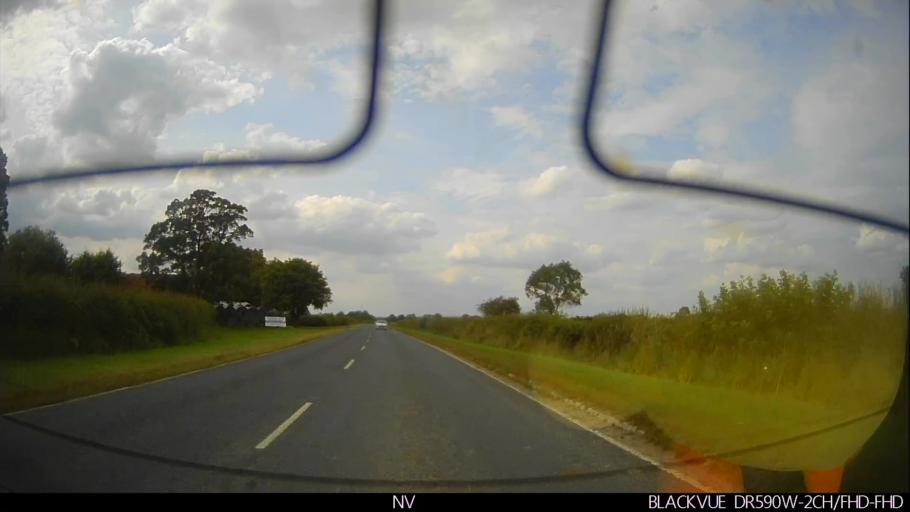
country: GB
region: England
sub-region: North Yorkshire
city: Marishes
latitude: 54.1971
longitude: -0.7662
